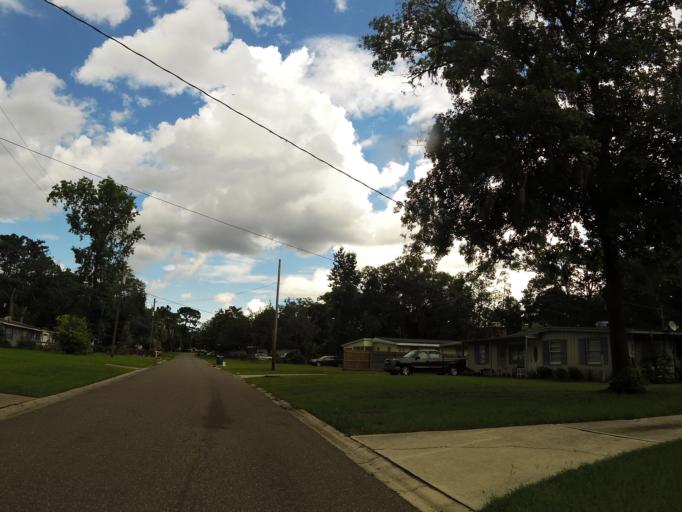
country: US
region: Florida
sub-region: Duval County
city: Jacksonville
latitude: 30.4220
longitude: -81.6717
